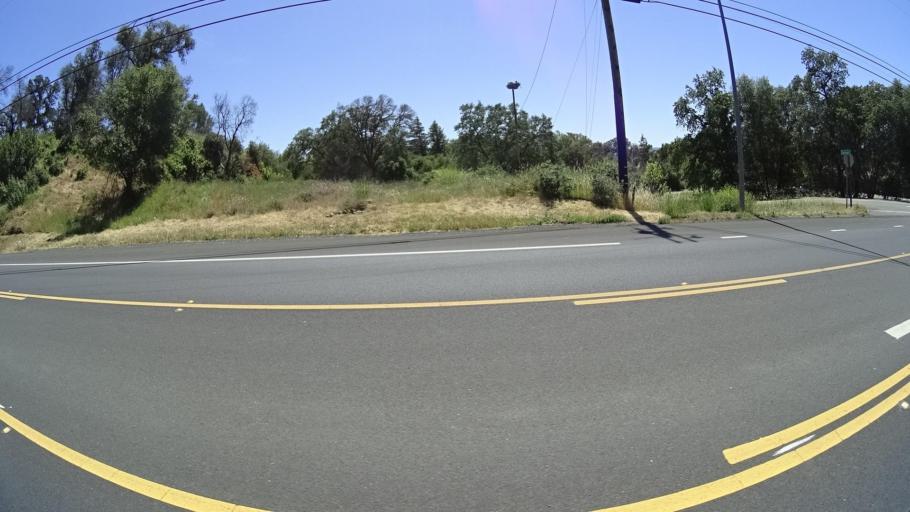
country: US
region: California
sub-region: Lake County
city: Nice
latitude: 39.1232
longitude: -122.8577
